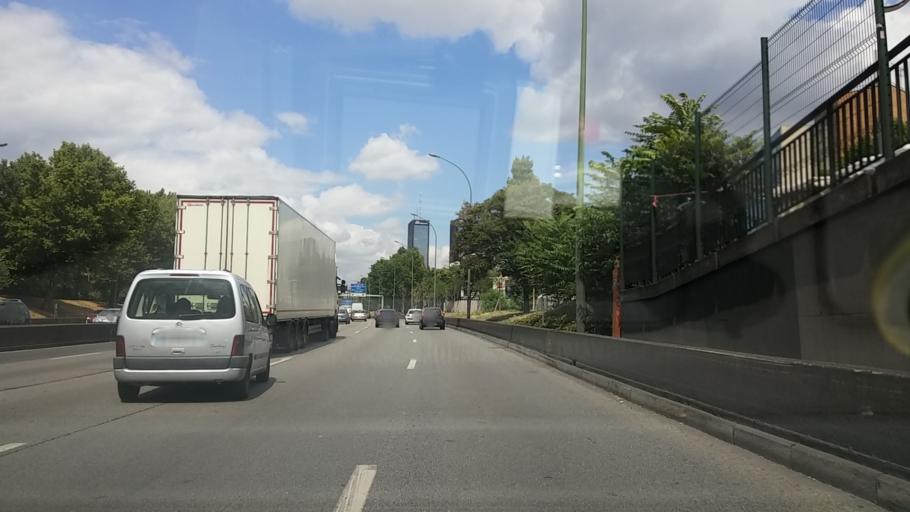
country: FR
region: Ile-de-France
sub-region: Departement de Seine-Saint-Denis
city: Bagnolet
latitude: 48.8581
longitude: 2.4141
